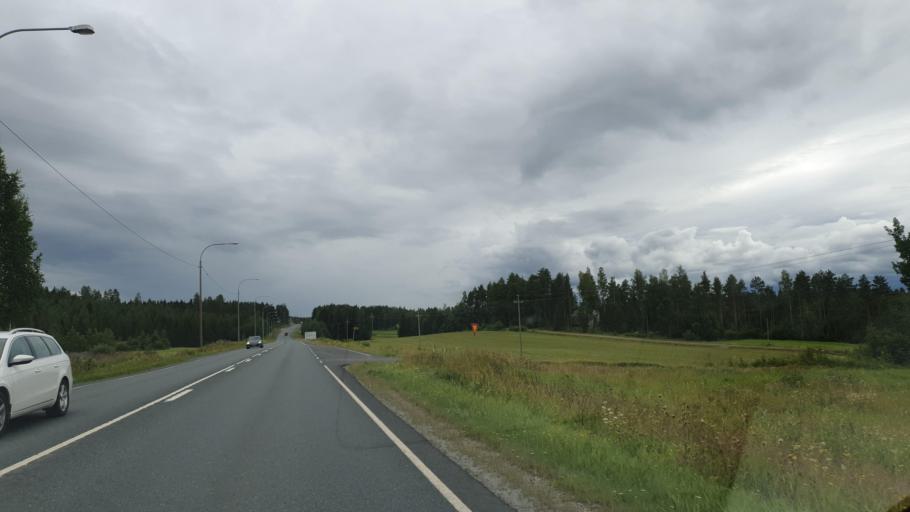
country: FI
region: Northern Savo
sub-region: Ylae-Savo
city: Lapinlahti
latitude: 63.3147
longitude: 27.4462
